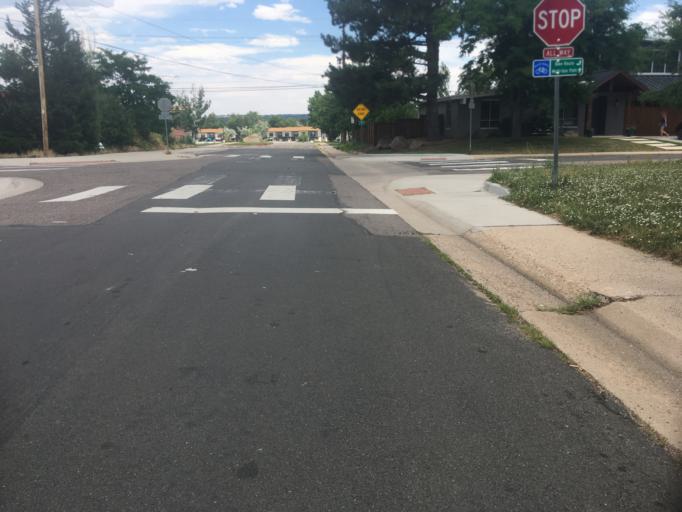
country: US
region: Colorado
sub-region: Boulder County
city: Boulder
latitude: 39.9822
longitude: -105.2420
